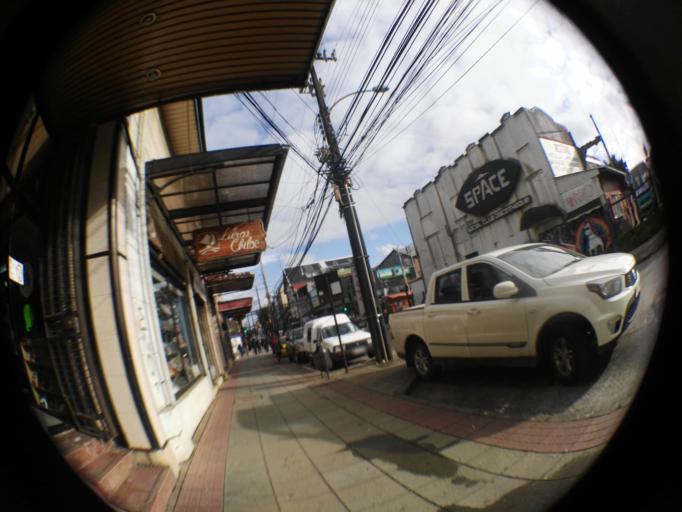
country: CL
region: Los Rios
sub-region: Provincia de Valdivia
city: Valdivia
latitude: -39.8130
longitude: -73.2436
